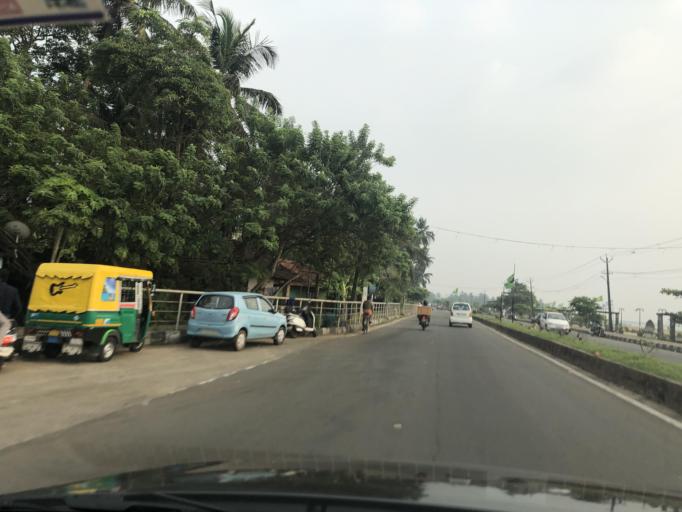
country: IN
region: Kerala
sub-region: Kozhikode
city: Kozhikode
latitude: 11.2791
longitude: 75.7626
